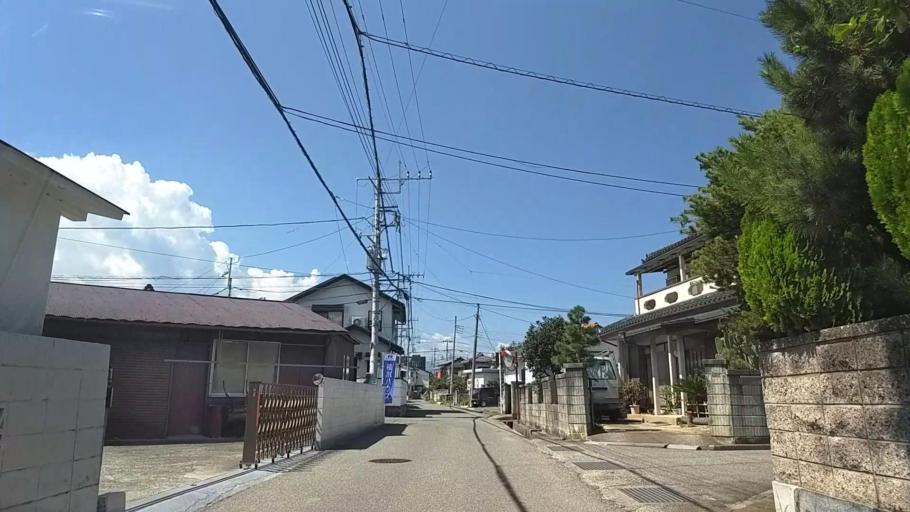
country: JP
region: Yamanashi
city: Ryuo
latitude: 35.6612
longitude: 138.5242
